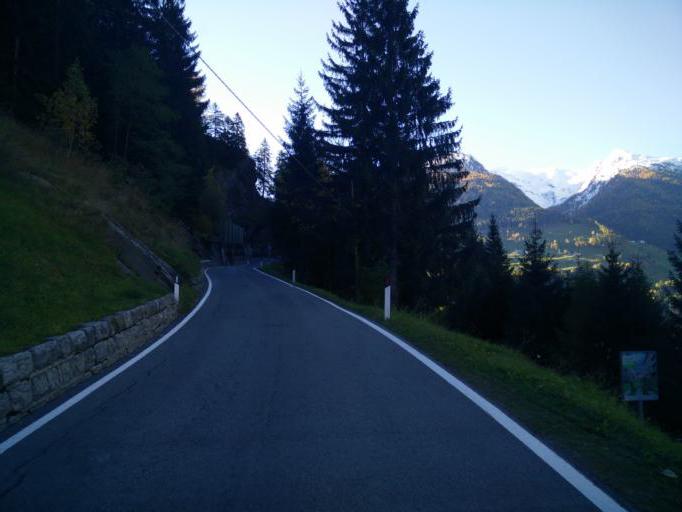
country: IT
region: Trentino-Alto Adige
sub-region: Bolzano
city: Moso in Passiria
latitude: 46.8360
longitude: 11.1682
